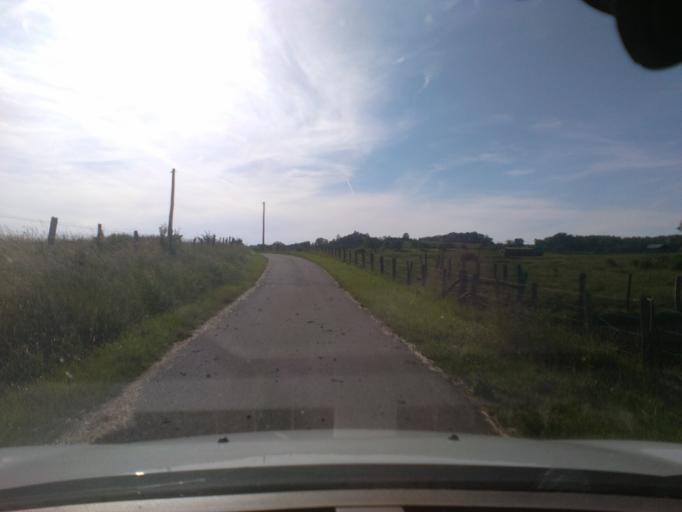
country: FR
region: Lorraine
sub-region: Departement des Vosges
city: Mirecourt
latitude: 48.2585
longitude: 6.1995
